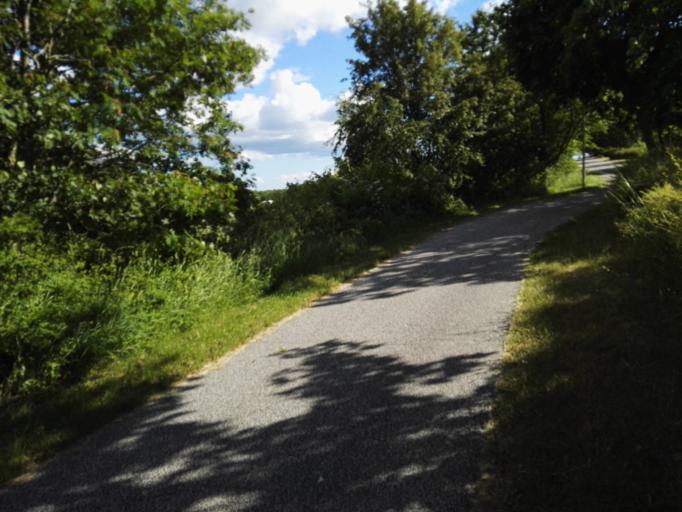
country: DK
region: Capital Region
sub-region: Egedal Kommune
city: Olstykke
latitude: 55.8081
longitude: 12.1647
